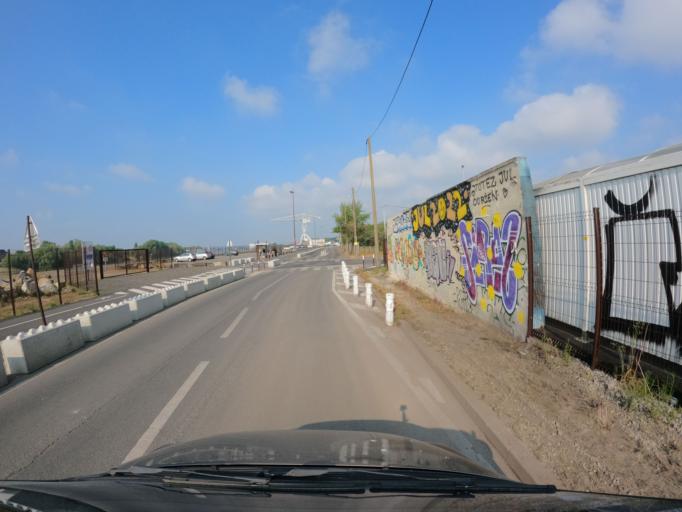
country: FR
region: Pays de la Loire
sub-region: Departement de la Loire-Atlantique
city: Nantes
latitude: 47.1996
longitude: -1.5684
